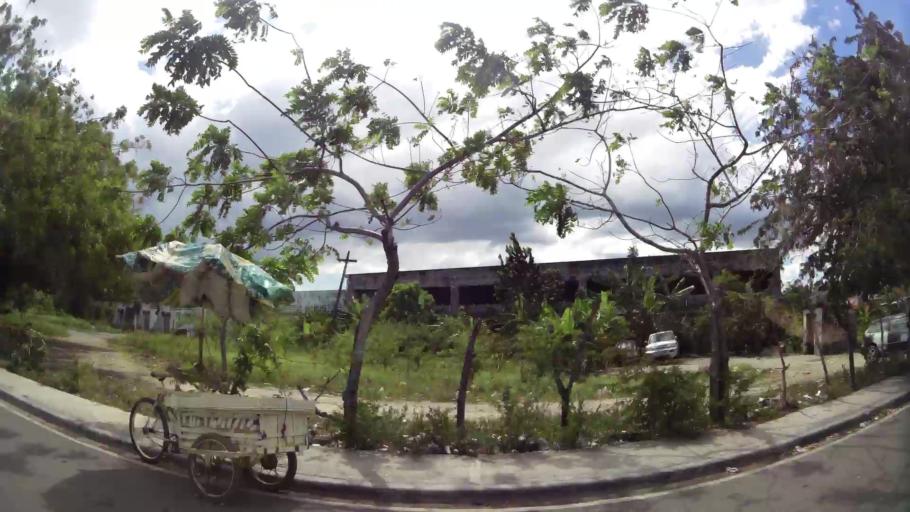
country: DO
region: San Cristobal
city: San Cristobal
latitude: 18.4222
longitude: -70.0947
